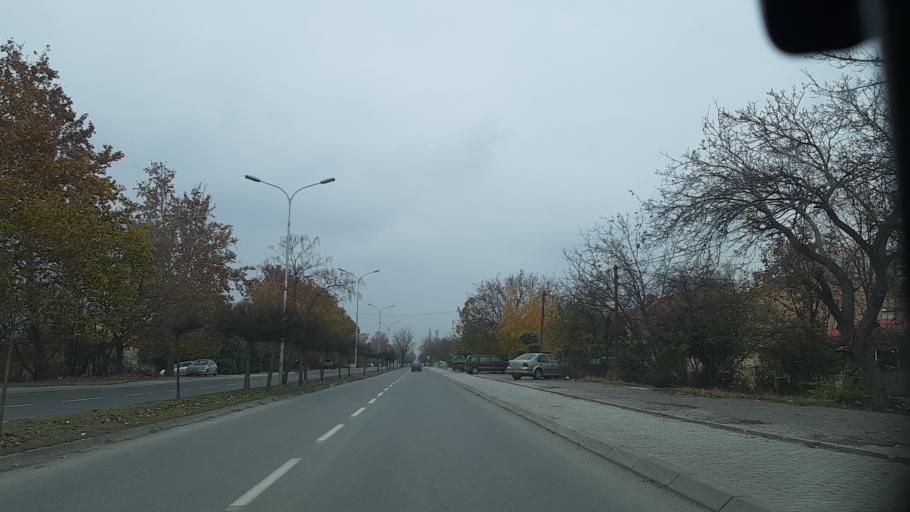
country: MK
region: Kisela Voda
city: Usje
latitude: 41.9718
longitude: 21.4766
